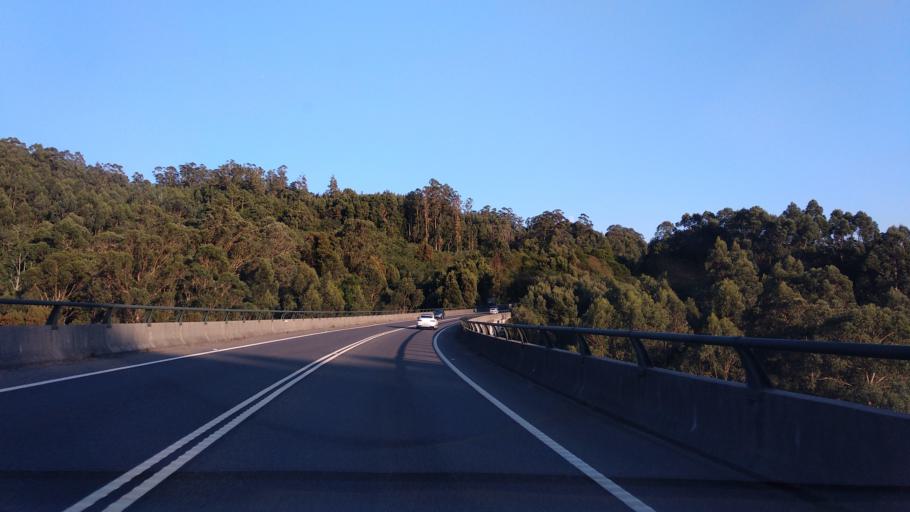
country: ES
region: Galicia
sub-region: Provincia de Pontevedra
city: Moana
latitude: 42.2885
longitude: -8.7717
